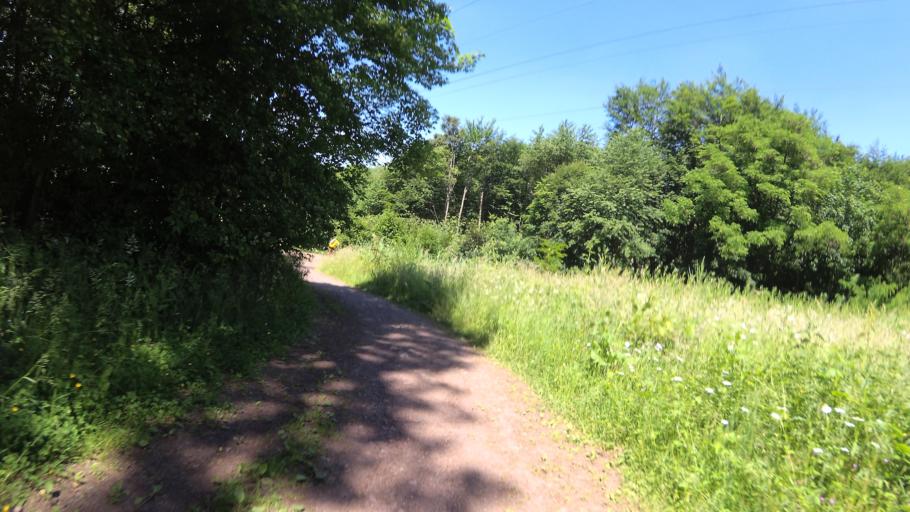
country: DE
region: Saarland
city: Lebach
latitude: 49.3703
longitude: 6.8714
